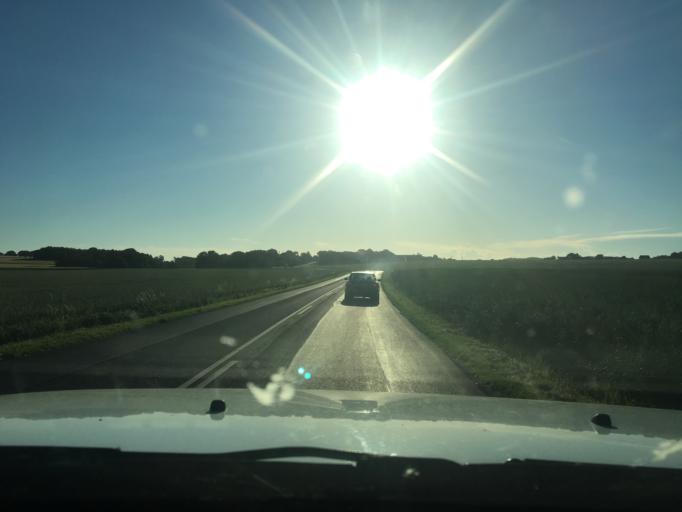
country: DK
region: Central Jutland
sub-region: Randers Kommune
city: Langa
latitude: 56.3898
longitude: 9.9415
